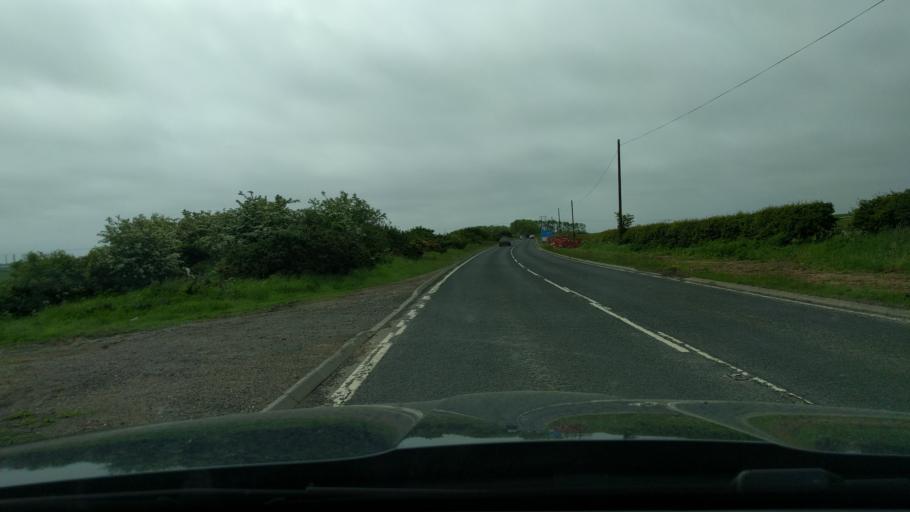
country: GB
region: England
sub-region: Northumberland
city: East Chevington
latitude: 55.2401
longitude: -1.5927
